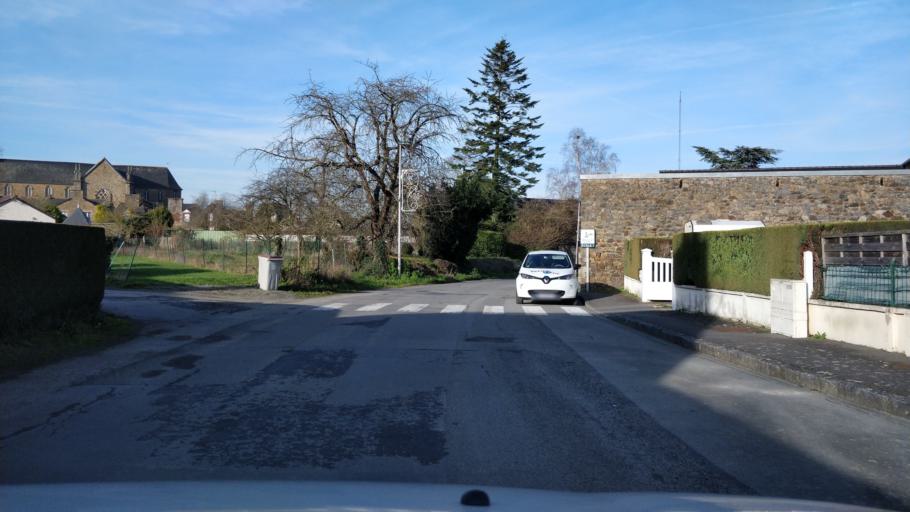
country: FR
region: Brittany
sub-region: Departement d'Ille-et-Vilaine
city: Plerguer
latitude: 48.5266
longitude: -1.8458
